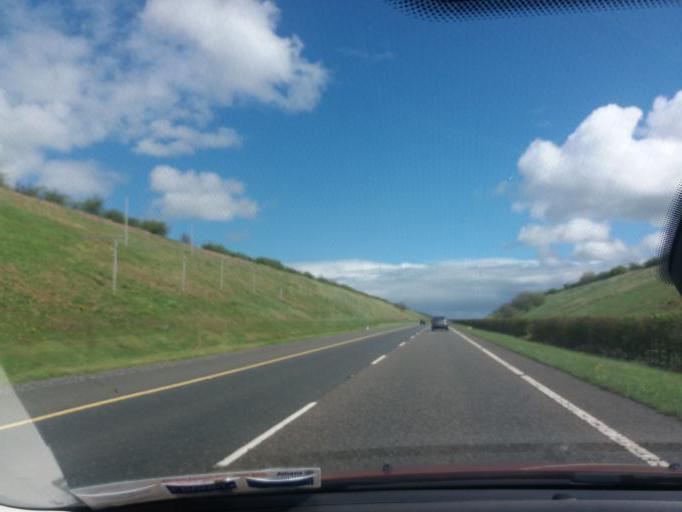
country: IE
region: Leinster
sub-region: Kildare
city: Kildare
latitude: 53.1549
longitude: -6.8751
